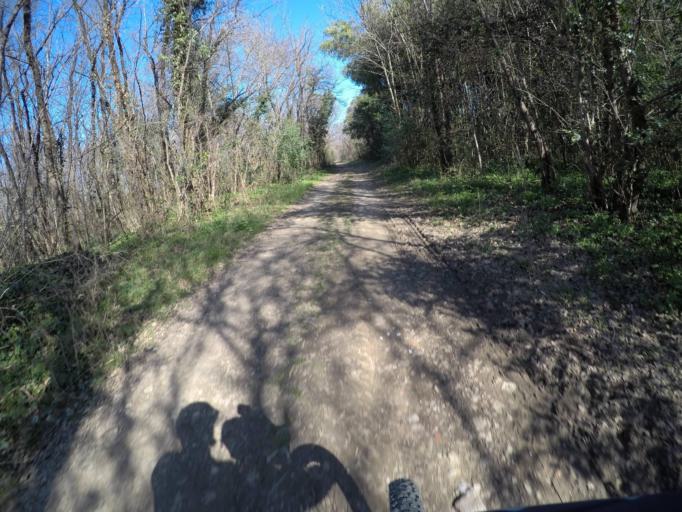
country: IT
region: Friuli Venezia Giulia
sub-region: Provincia di Udine
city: Zugliano-Terenzano-Cargnacco
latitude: 46.0145
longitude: 13.2021
